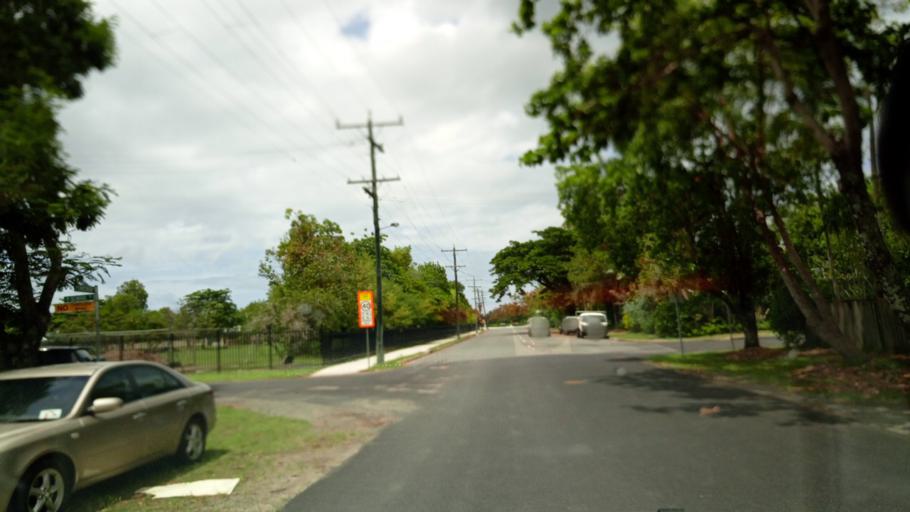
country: AU
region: Queensland
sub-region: Cairns
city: Redlynch
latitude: -16.8543
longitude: 145.7456
